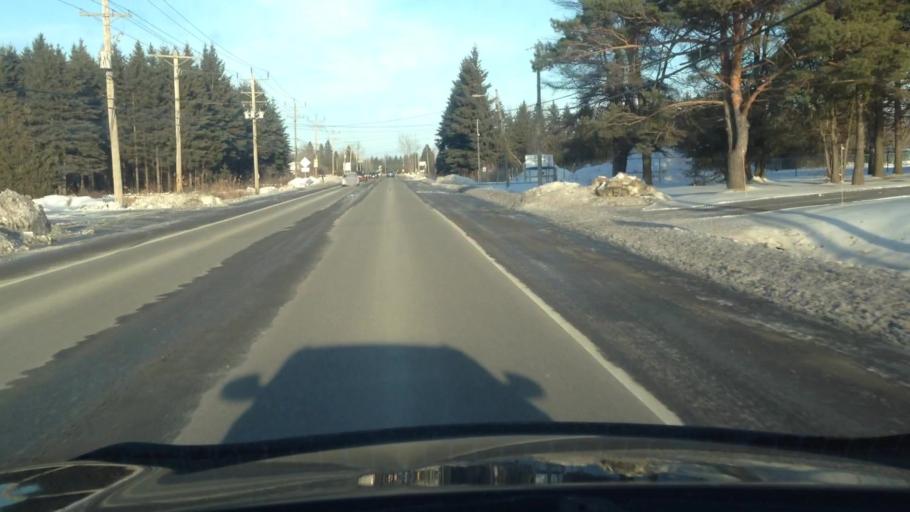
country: CA
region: Quebec
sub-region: Laurentides
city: Sainte-Sophie
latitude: 45.8053
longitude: -73.9290
